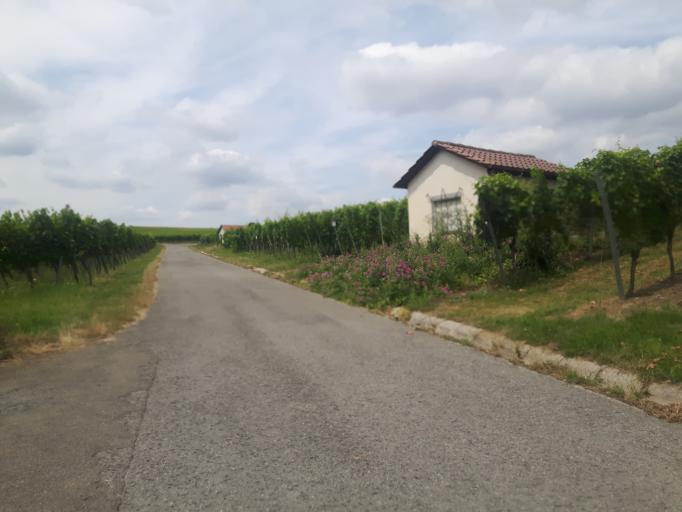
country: DE
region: Baden-Wuerttemberg
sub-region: Regierungsbezirk Stuttgart
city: Bonnigheim
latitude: 49.0402
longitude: 9.0760
